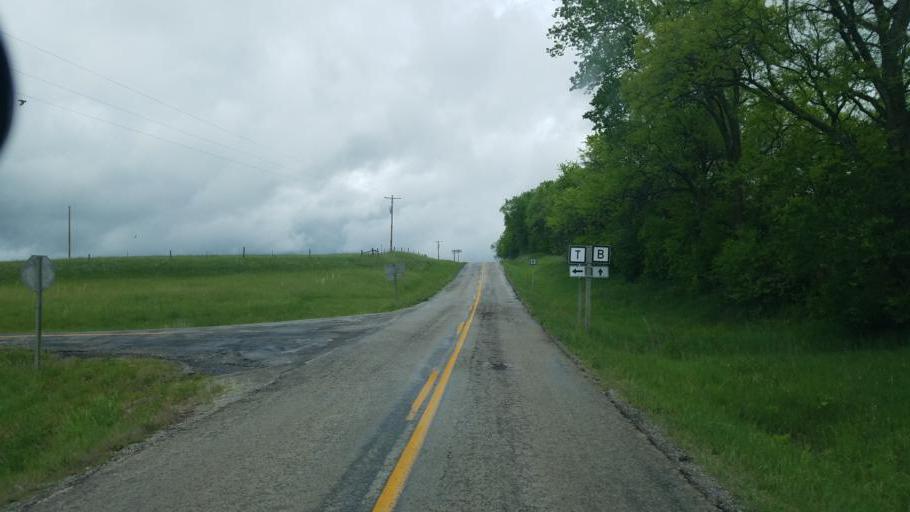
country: US
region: Missouri
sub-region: Mercer County
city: Princeton
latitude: 40.5269
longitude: -93.7178
